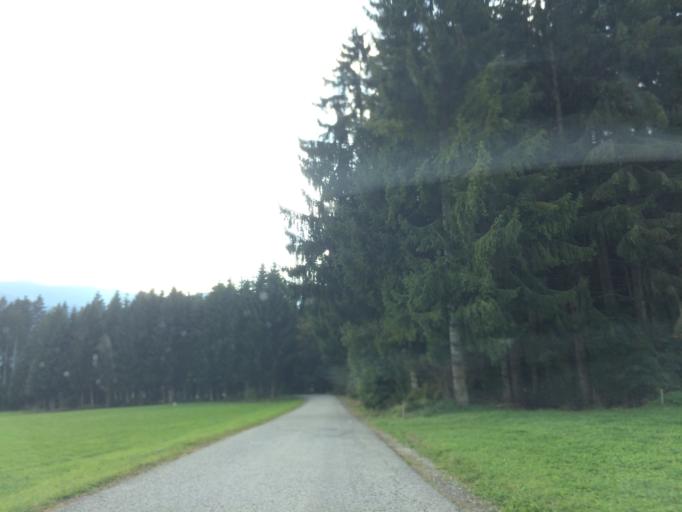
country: AT
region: Styria
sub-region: Politischer Bezirk Murtal
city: Seckau
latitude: 47.2735
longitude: 14.7522
